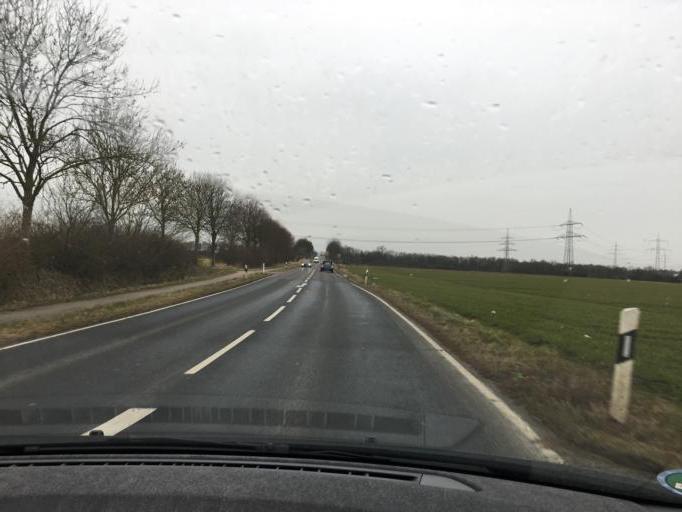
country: DE
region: North Rhine-Westphalia
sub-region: Regierungsbezirk Koln
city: Bergheim
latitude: 50.9371
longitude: 6.6229
